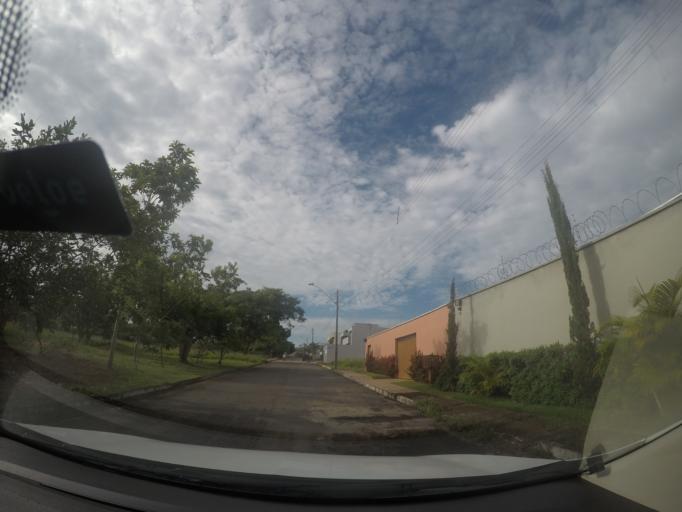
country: BR
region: Goias
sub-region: Goiania
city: Goiania
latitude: -16.6789
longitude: -49.2018
